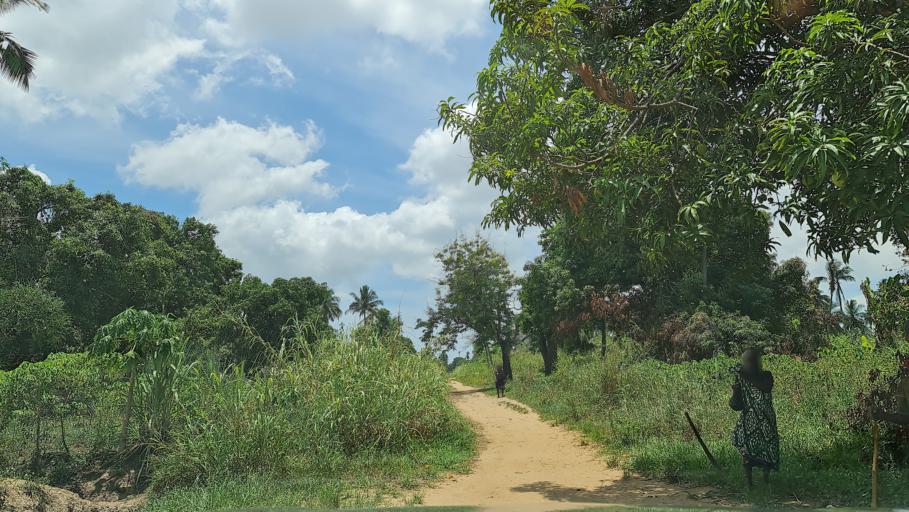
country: MZ
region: Zambezia
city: Quelimane
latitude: -17.5719
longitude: 37.3736
